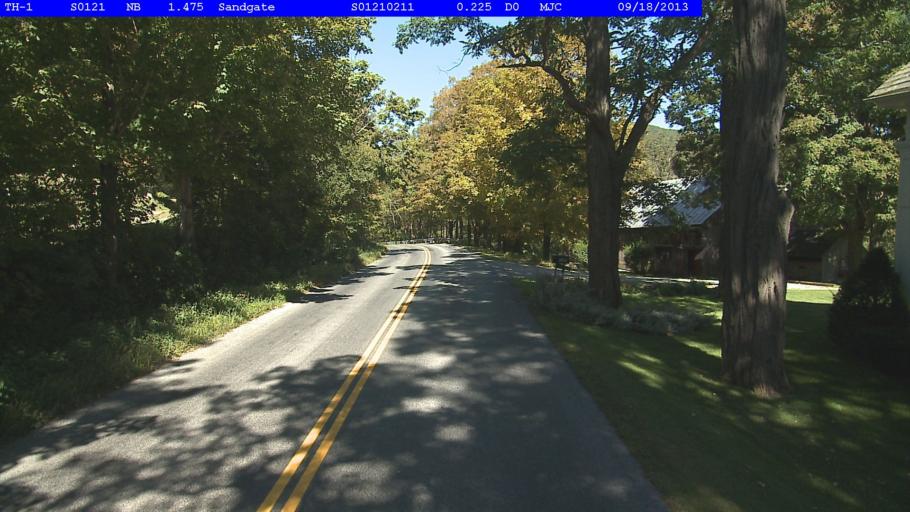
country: US
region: Vermont
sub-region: Bennington County
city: Arlington
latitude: 43.1238
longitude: -73.2064
